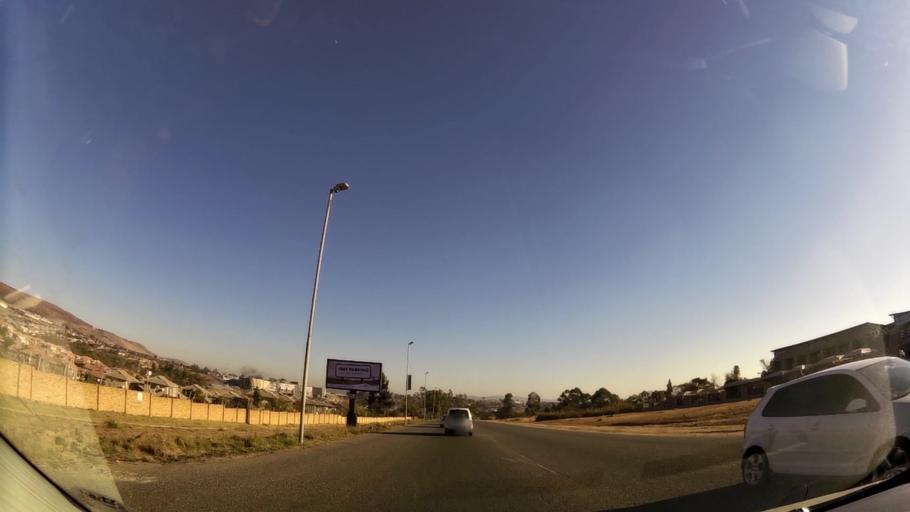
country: ZA
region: Gauteng
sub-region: West Rand District Municipality
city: Muldersdriseloop
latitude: -26.0663
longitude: 27.8477
